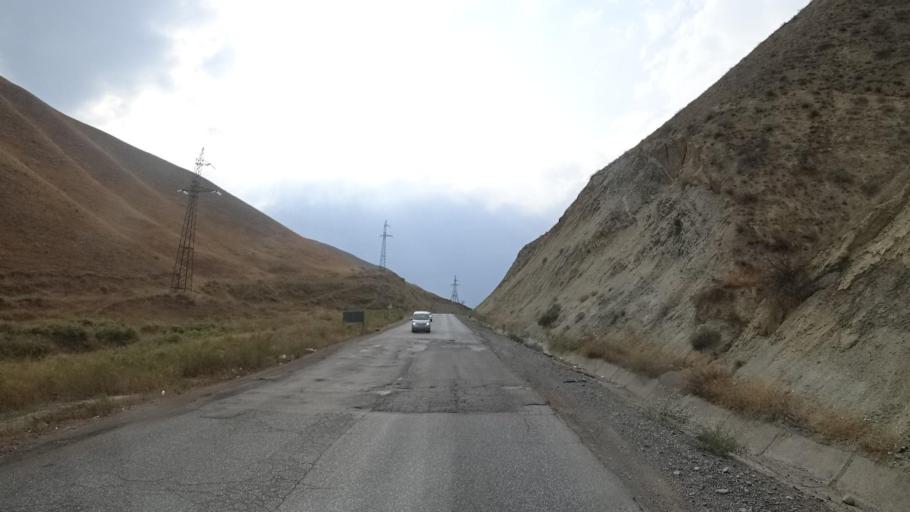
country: KG
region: Jalal-Abad
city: Uch-Terek
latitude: 41.8196
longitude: 73.1875
